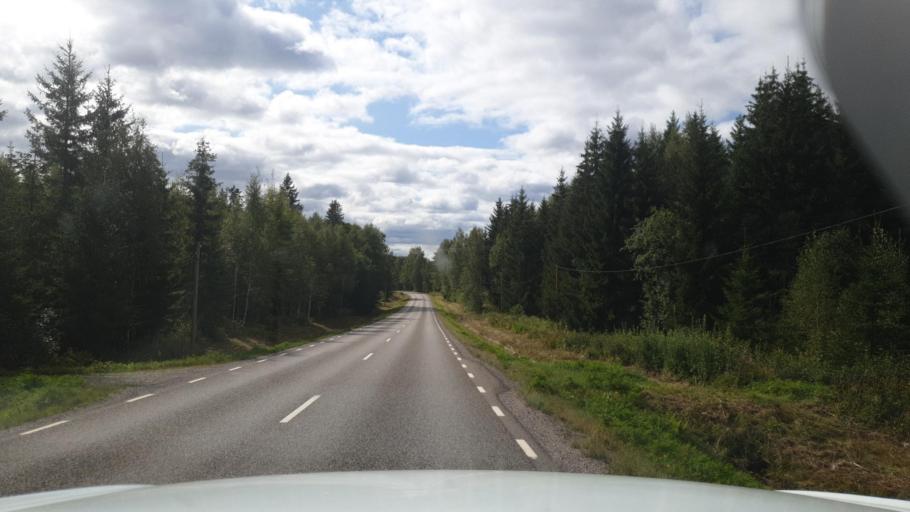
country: SE
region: Vaermland
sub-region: Eda Kommun
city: Amotfors
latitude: 59.6996
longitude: 12.4302
